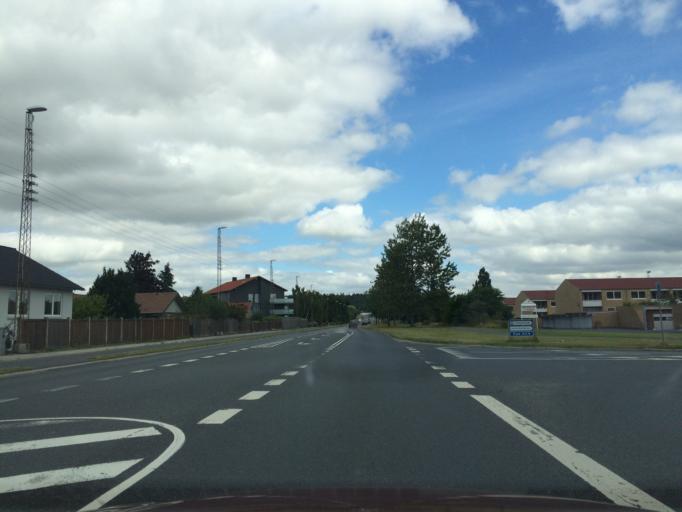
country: DK
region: Central Jutland
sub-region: Silkeborg Kommune
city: Silkeborg
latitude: 56.1807
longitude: 9.5676
